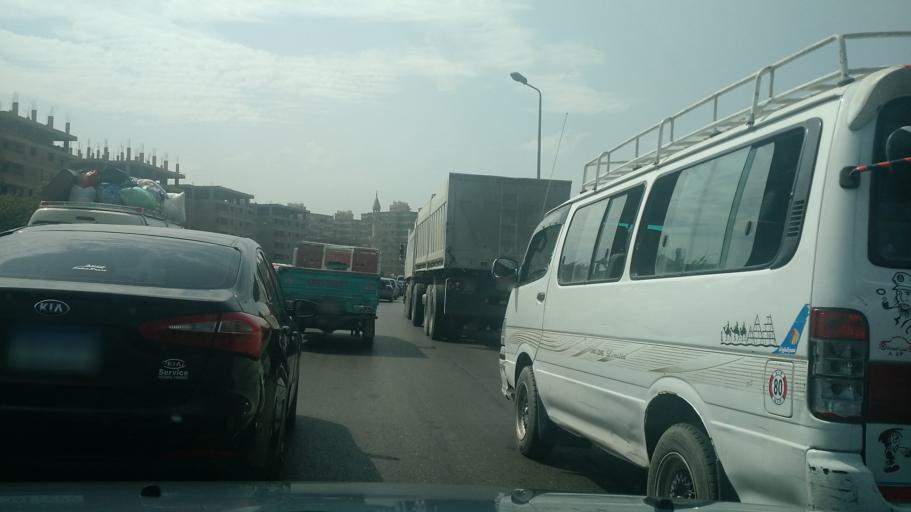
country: EG
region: Al Jizah
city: Al Jizah
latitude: 29.9884
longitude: 31.2872
